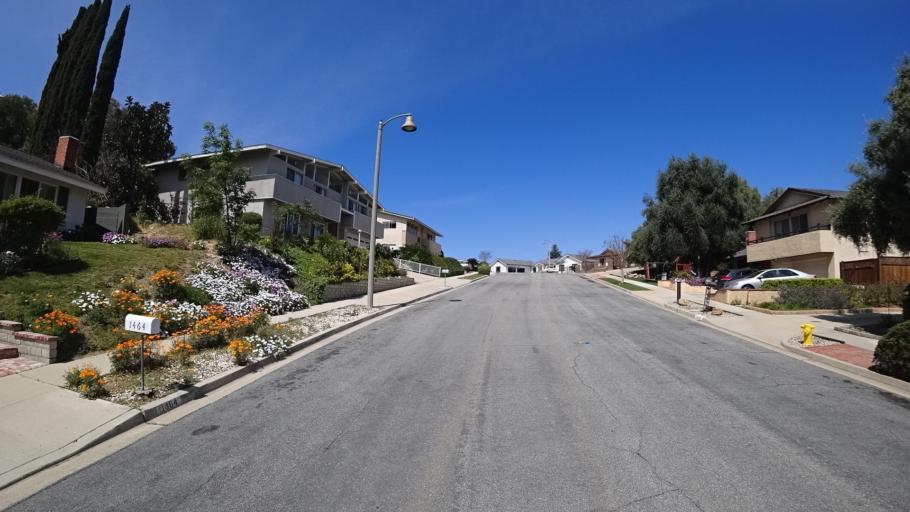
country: US
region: California
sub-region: Ventura County
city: Moorpark
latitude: 34.2404
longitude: -118.8519
